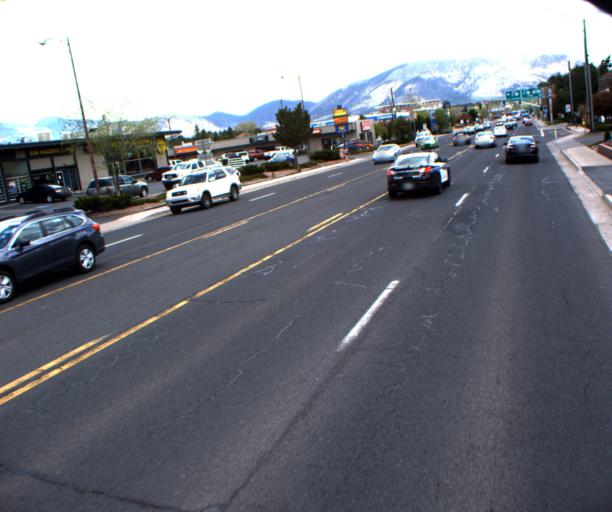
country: US
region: Arizona
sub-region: Coconino County
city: Flagstaff
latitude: 35.1916
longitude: -111.6599
